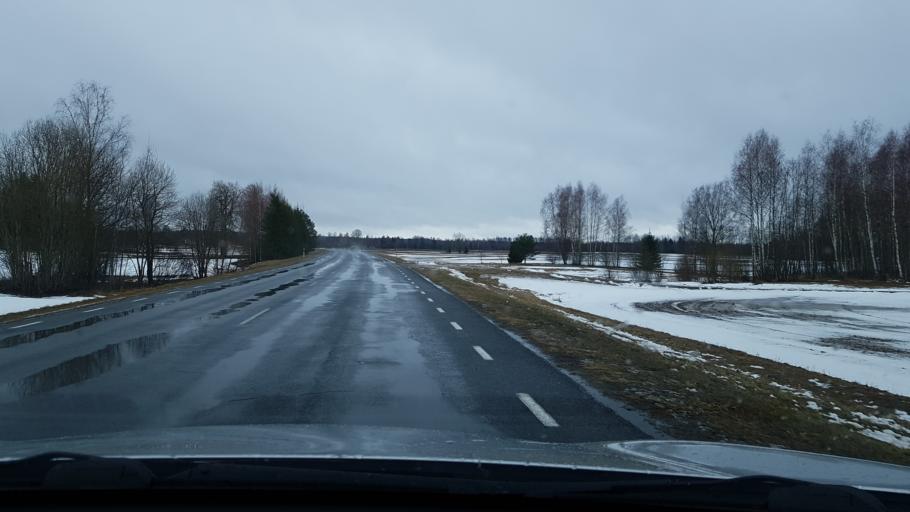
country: LV
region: Apes Novads
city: Ape
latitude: 57.6880
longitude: 26.7261
